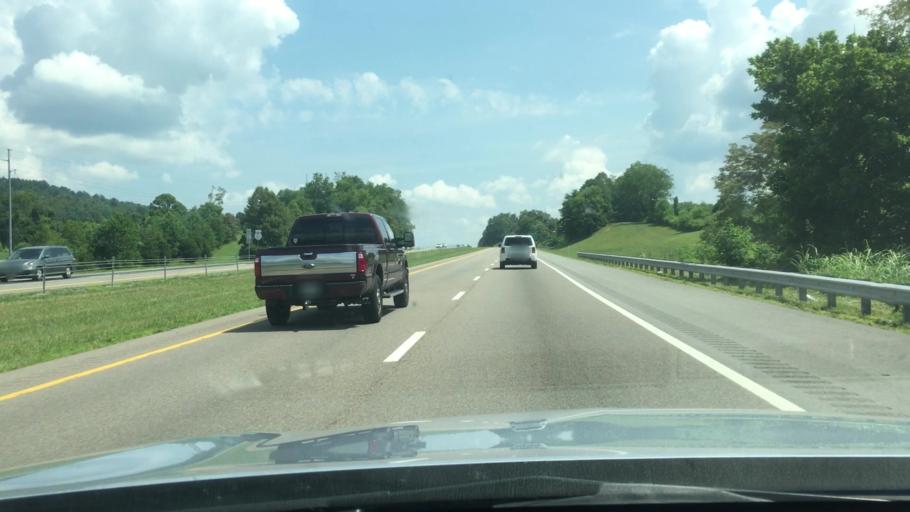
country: US
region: Tennessee
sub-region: Unicoi County
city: Unicoi
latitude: 36.2007
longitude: -82.3604
